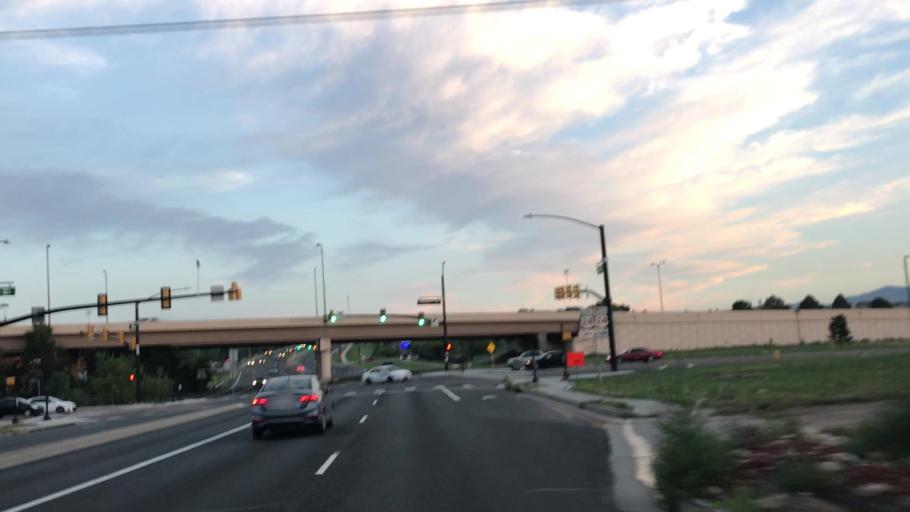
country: US
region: Colorado
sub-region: El Paso County
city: Colorado Springs
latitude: 38.8181
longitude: -104.7807
